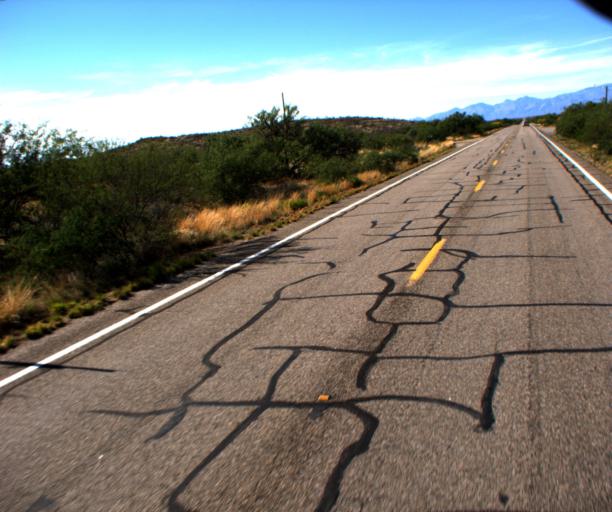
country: US
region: Arizona
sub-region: Pima County
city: Corona de Tucson
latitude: 31.9446
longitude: -110.6644
